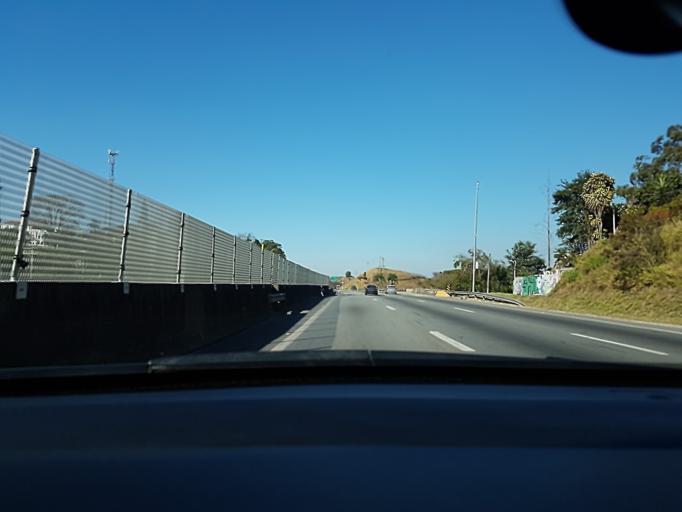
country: BR
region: Sao Paulo
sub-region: Aruja
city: Aruja
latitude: -23.4027
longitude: -46.3183
